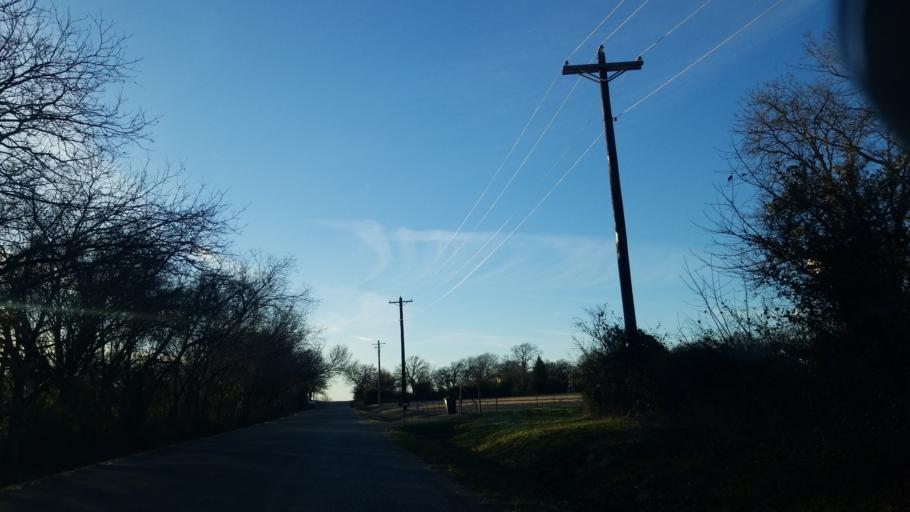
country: US
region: Texas
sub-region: Denton County
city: Denton
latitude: 33.1831
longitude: -97.1447
